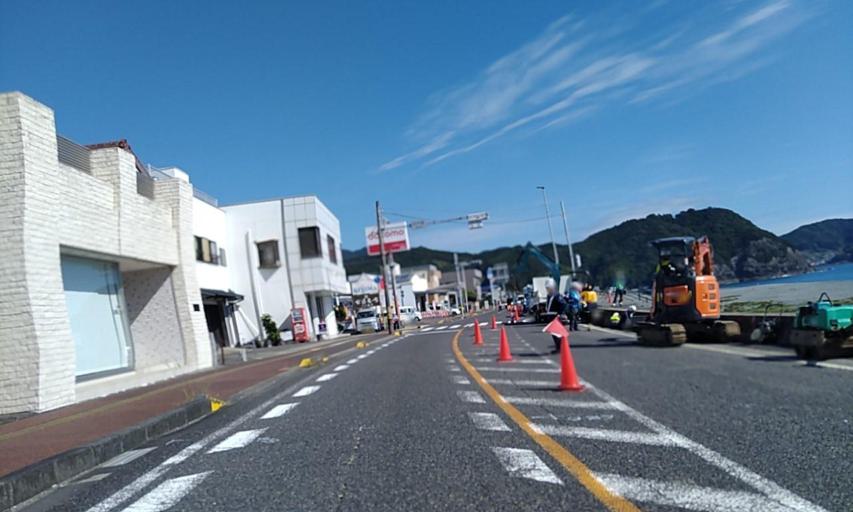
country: JP
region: Wakayama
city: Shingu
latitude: 33.8851
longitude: 136.0982
